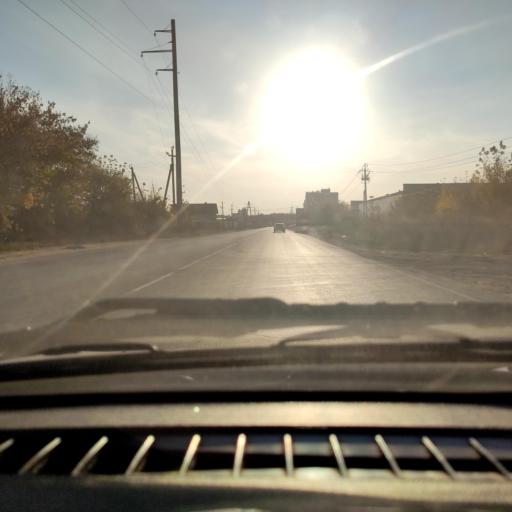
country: RU
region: Samara
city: Zhigulevsk
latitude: 53.5266
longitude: 49.4801
